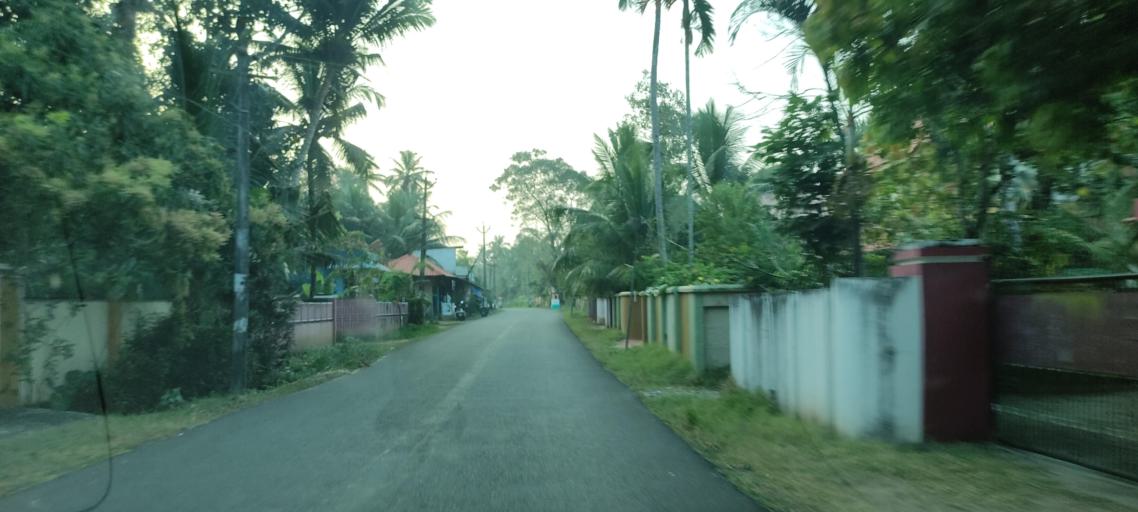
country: IN
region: Kerala
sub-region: Alappuzha
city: Kattanam
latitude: 9.1351
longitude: 76.5375
